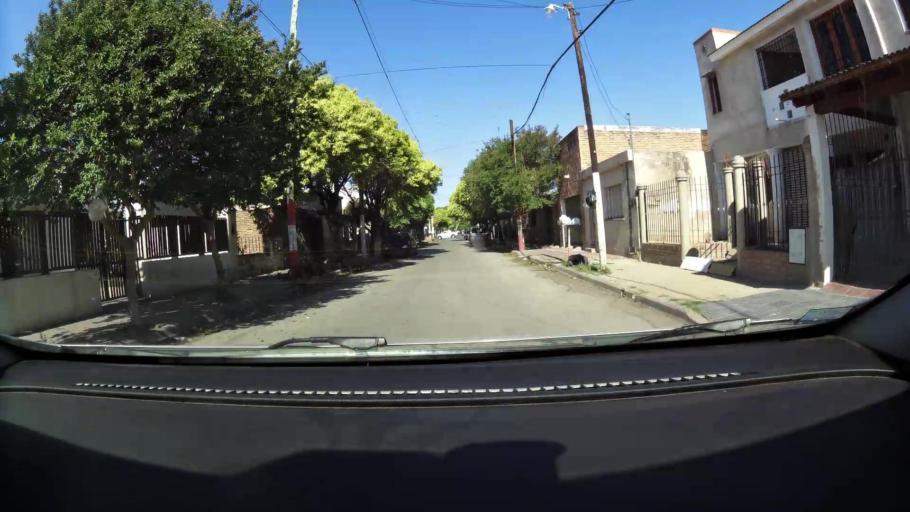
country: AR
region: Cordoba
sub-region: Departamento de Capital
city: Cordoba
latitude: -31.3744
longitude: -64.1848
